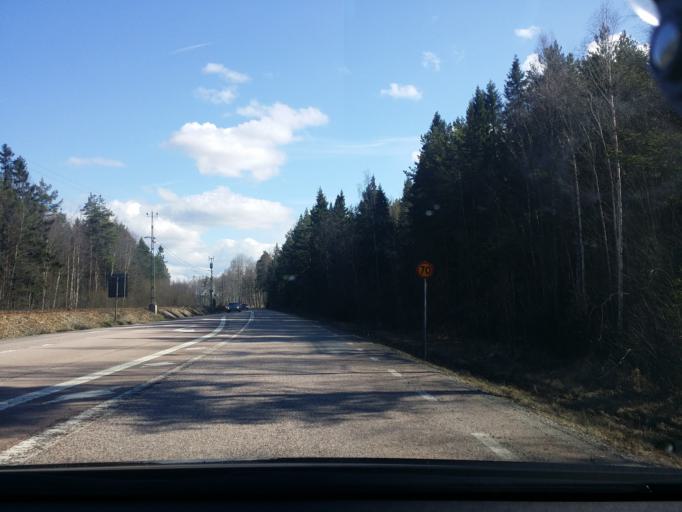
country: SE
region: Vaestmanland
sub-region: Sala Kommun
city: Sala
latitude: 59.9673
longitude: 16.5056
